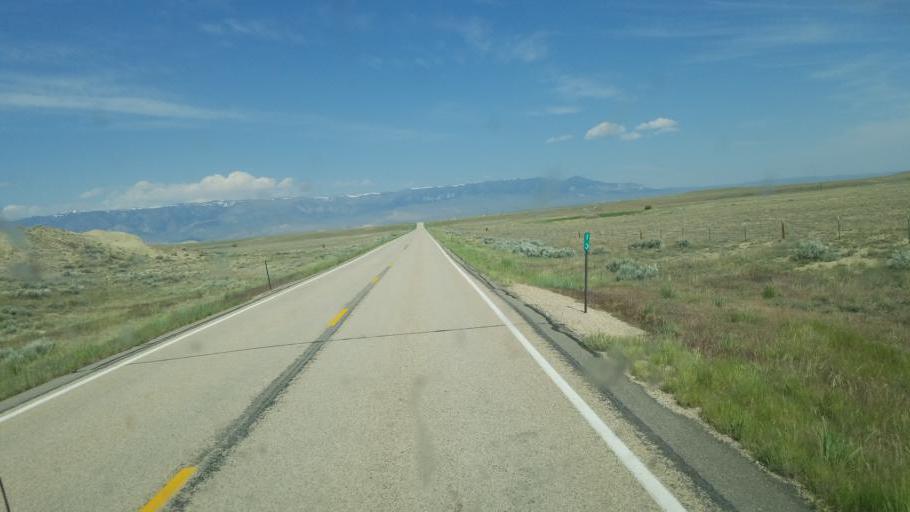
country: US
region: Wyoming
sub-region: Park County
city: Powell
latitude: 44.8507
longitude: -109.0098
